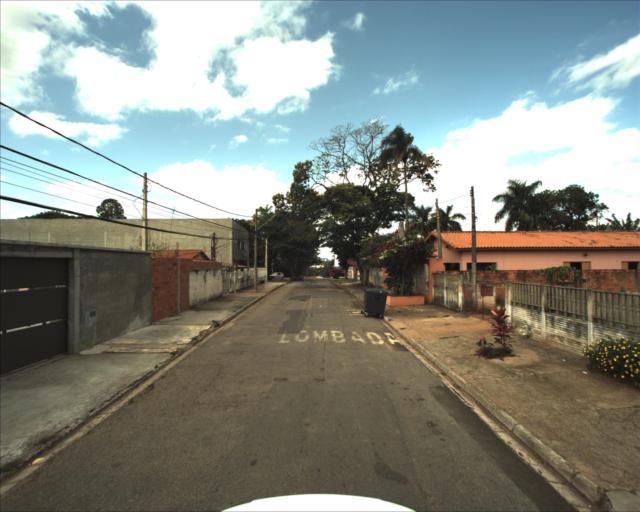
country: BR
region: Sao Paulo
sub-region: Sorocaba
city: Sorocaba
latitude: -23.3982
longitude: -47.3780
